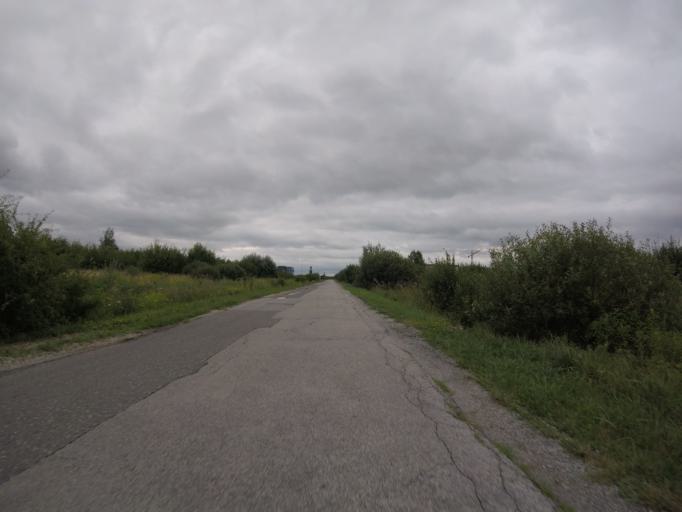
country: HR
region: Zagrebacka
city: Turopolje
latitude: 45.6555
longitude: 16.1295
